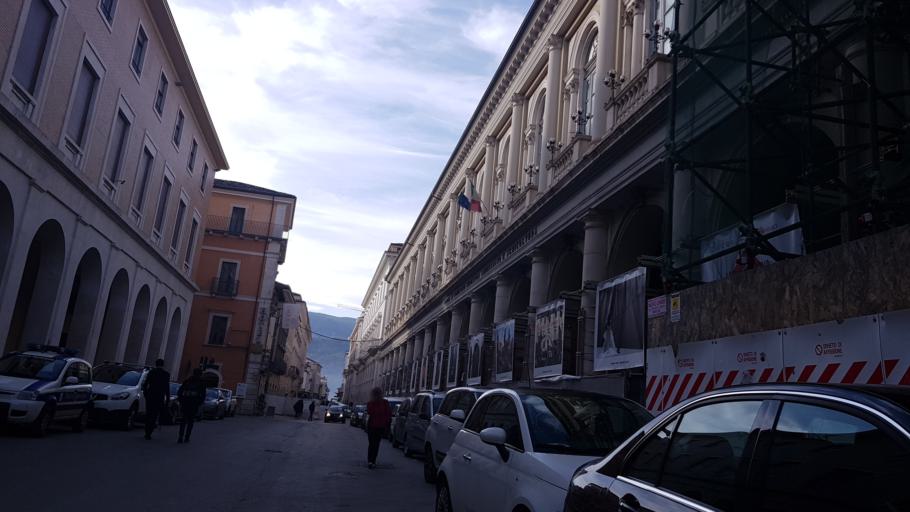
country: IT
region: Abruzzo
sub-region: Provincia dell' Aquila
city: L'Aquila
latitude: 42.3497
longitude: 13.3973
